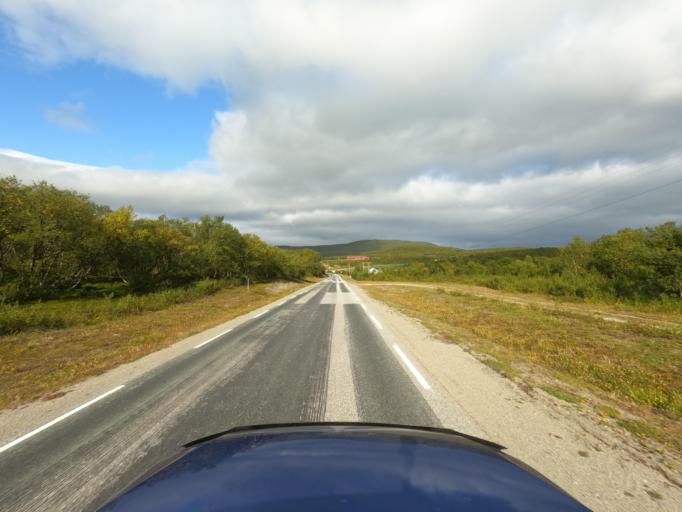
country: NO
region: Finnmark Fylke
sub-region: Porsanger
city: Lakselv
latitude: 70.2612
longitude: 25.0264
